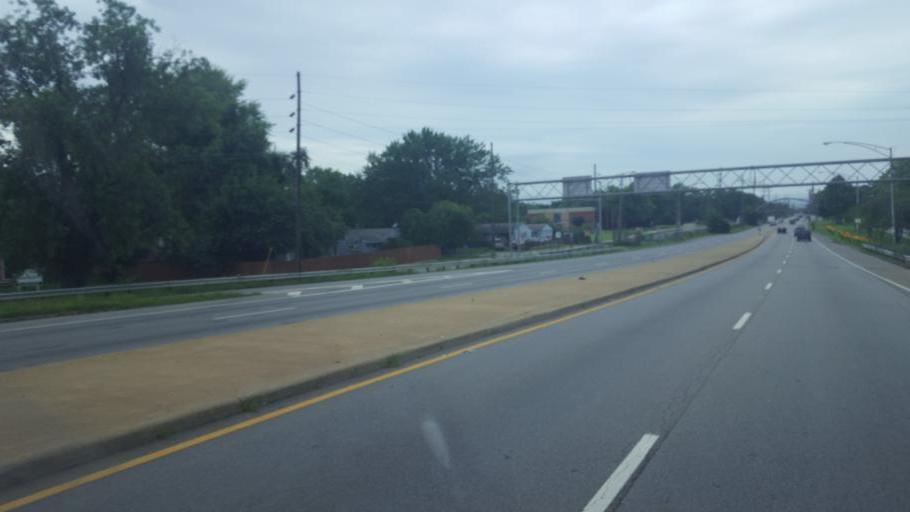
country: US
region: Ohio
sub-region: Franklin County
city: Whitehall
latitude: 39.9377
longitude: -82.8785
